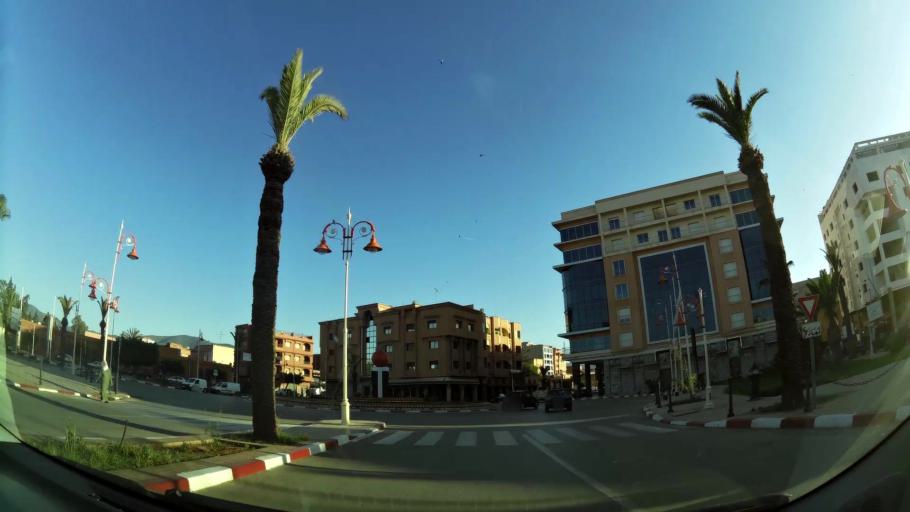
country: MA
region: Oriental
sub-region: Berkane-Taourirt
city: Berkane
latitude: 34.9283
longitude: -2.3299
